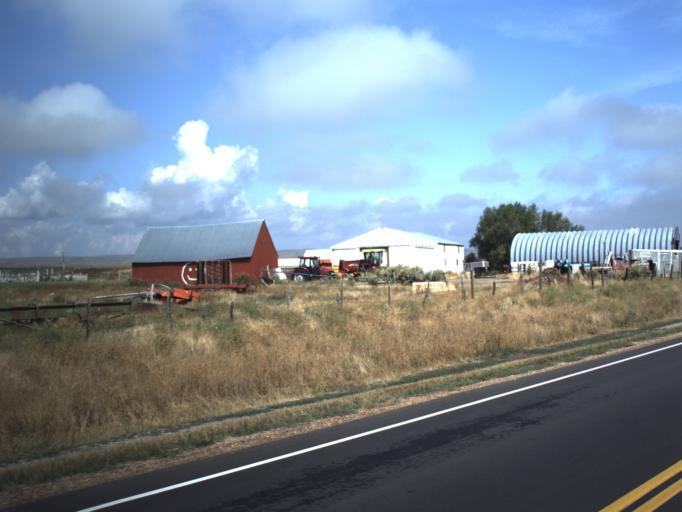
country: US
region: Utah
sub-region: Rich County
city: Randolph
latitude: 41.7040
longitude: -111.1600
